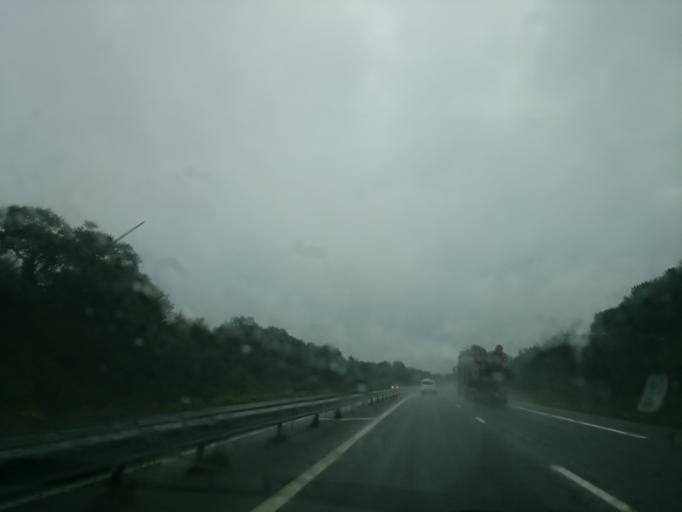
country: FR
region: Pays de la Loire
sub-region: Departement de la Loire-Atlantique
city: Prinquiau
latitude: 47.4115
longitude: -2.0206
